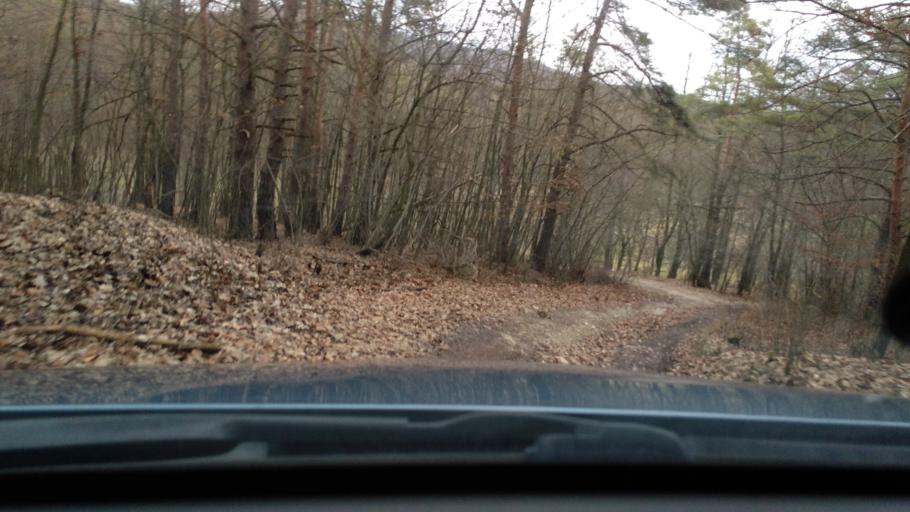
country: SK
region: Nitriansky
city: Trencianske Teplice
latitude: 48.8392
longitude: 18.1775
